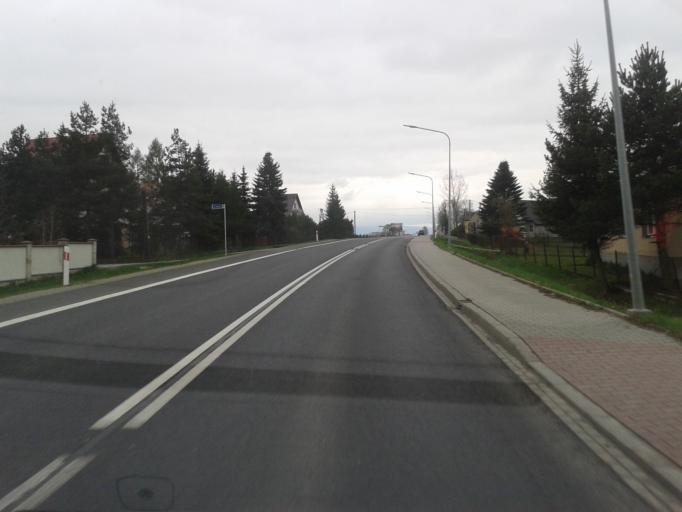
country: PL
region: Lesser Poland Voivodeship
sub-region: Powiat nowotarski
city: Jablonka
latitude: 49.4588
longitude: 19.6902
